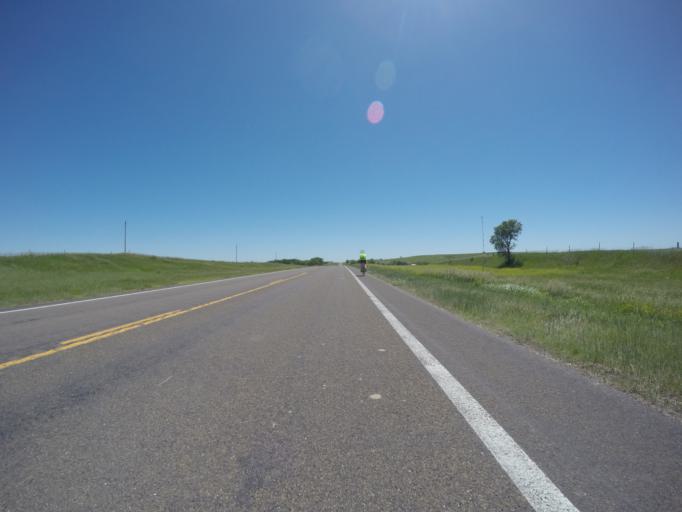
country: US
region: Kansas
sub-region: Phillips County
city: Phillipsburg
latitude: 39.8285
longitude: -99.6002
